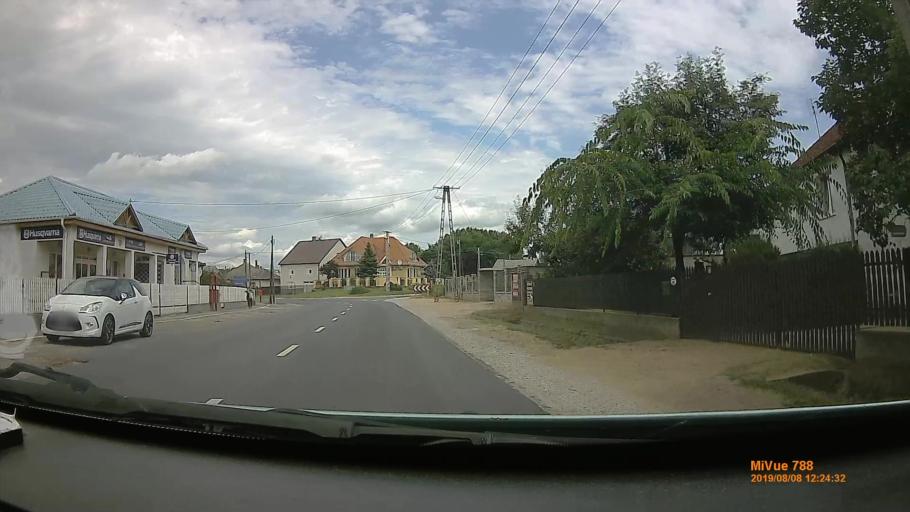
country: HU
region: Szabolcs-Szatmar-Bereg
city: Nyirbogat
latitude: 47.8051
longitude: 22.0655
